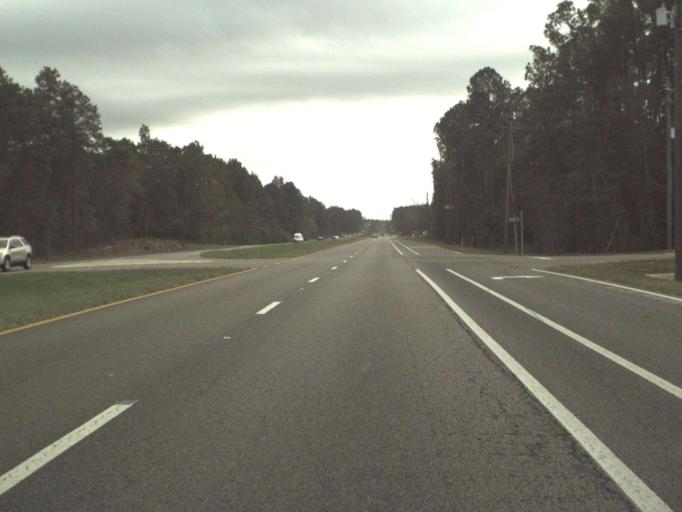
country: US
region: Florida
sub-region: Escambia County
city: Cantonment
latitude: 30.6434
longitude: -87.3457
